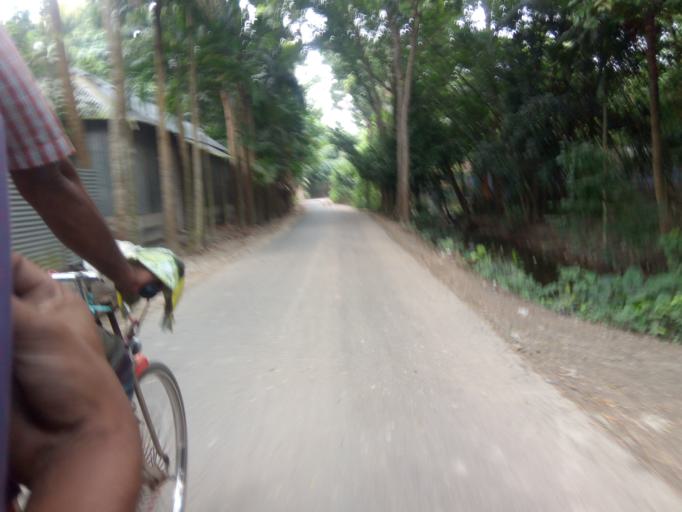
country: BD
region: Khulna
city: Kalia
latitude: 23.2162
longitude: 89.7030
